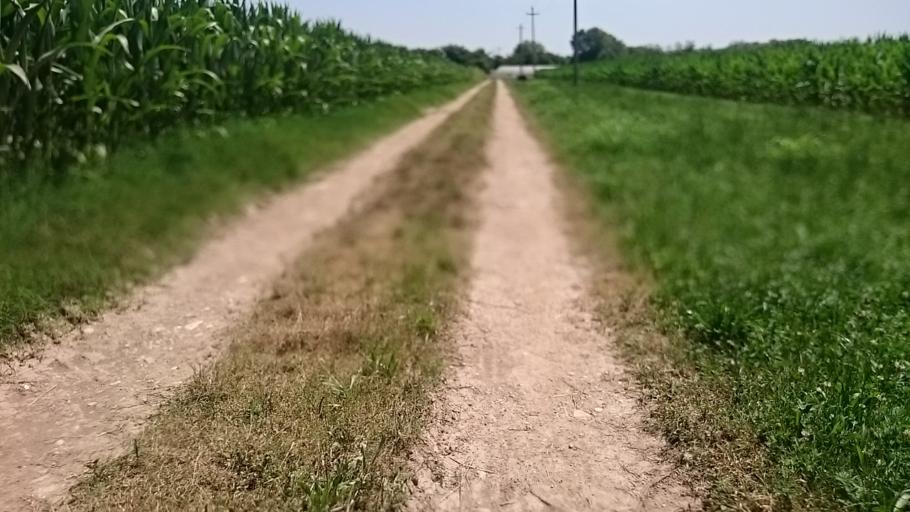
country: IT
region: Veneto
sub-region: Provincia di Vicenza
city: Vicenza
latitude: 45.5324
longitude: 11.5666
